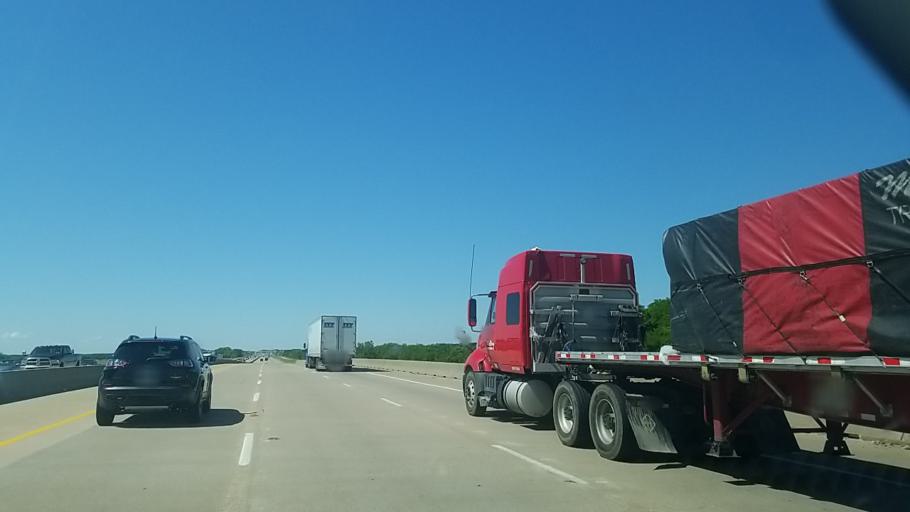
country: US
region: Texas
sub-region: Navarro County
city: Corsicana
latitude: 32.1638
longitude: -96.4692
